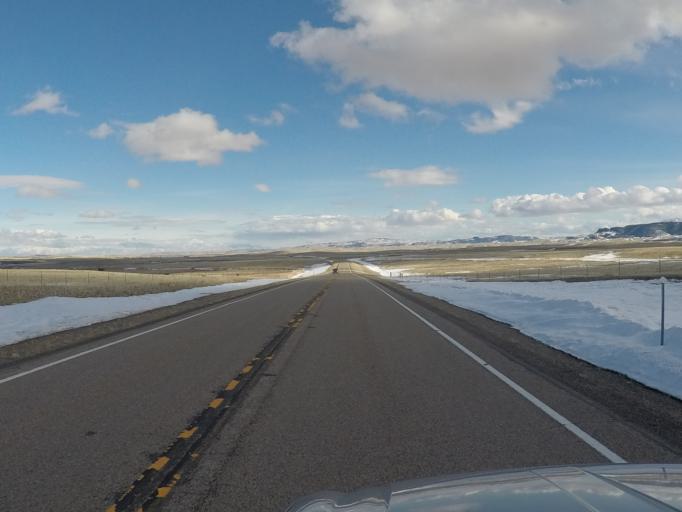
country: US
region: Montana
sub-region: Meagher County
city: White Sulphur Springs
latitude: 46.5131
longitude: -110.3945
